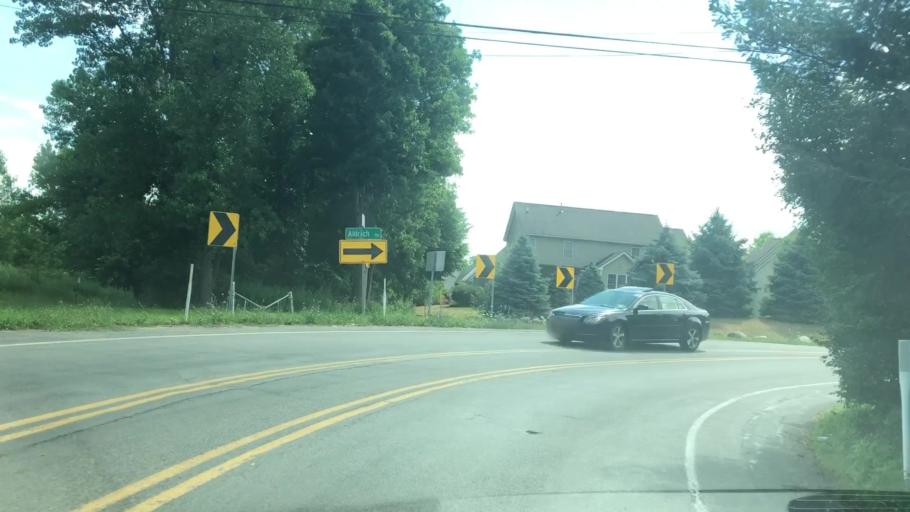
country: US
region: New York
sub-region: Monroe County
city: Fairport
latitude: 43.0795
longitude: -77.3924
